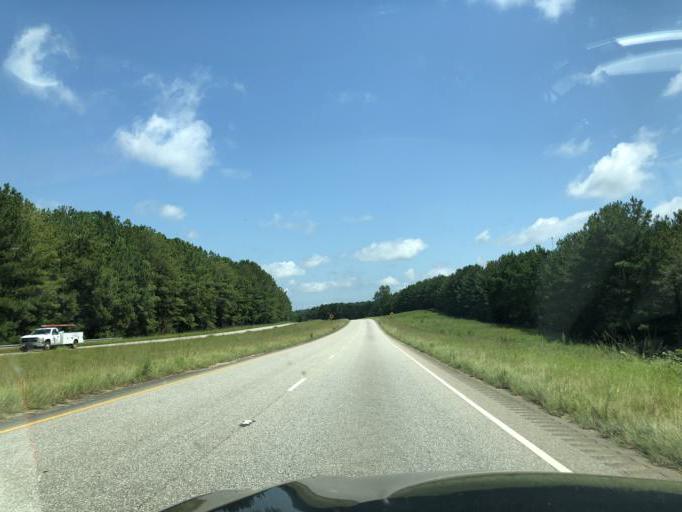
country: US
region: Alabama
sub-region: Henry County
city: Abbeville
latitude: 31.7269
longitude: -85.2592
